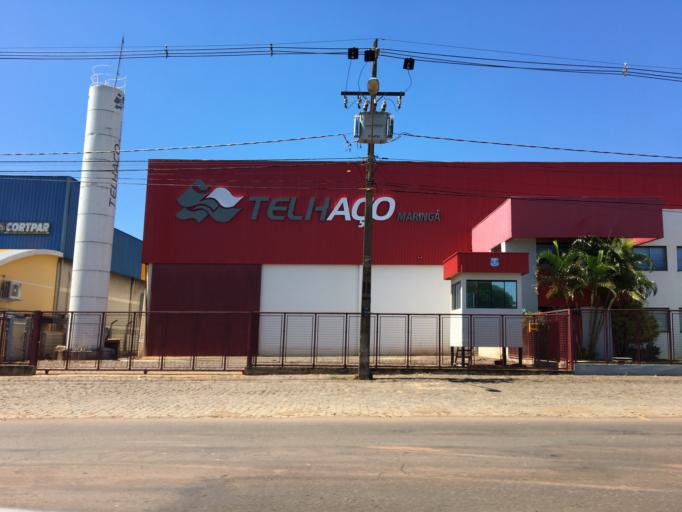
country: BR
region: Parana
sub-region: Maringa
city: Maringa
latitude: -23.4585
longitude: -51.9460
